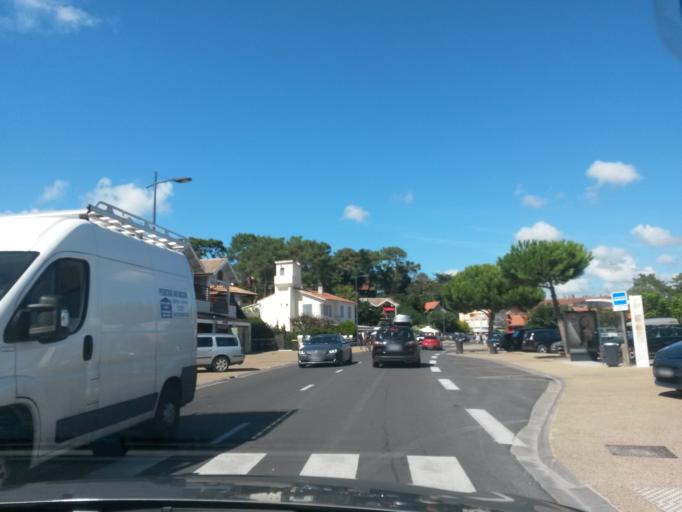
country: FR
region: Aquitaine
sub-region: Departement de la Gironde
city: Arcachon
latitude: 44.7003
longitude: -1.2299
